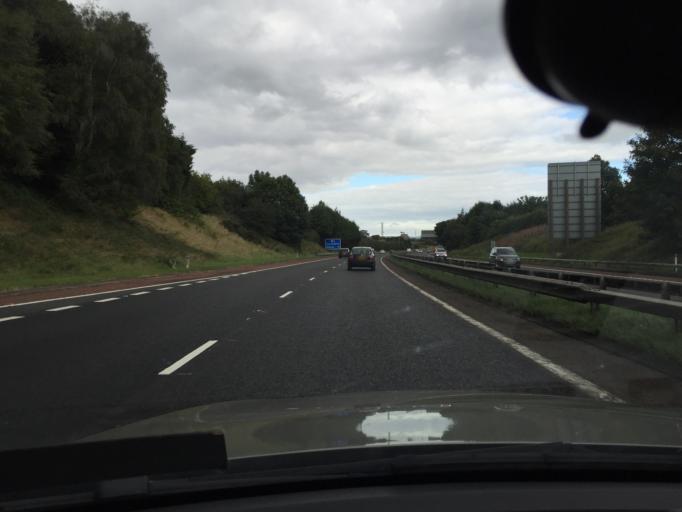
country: GB
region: Northern Ireland
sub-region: Lisburn District
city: Lisburn
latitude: 54.5087
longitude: -6.0246
